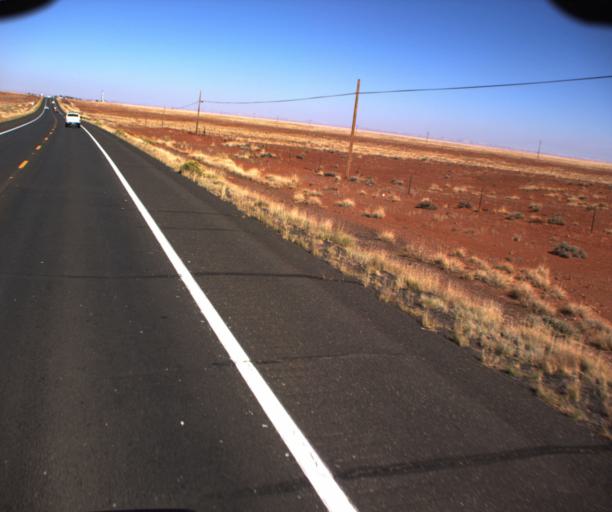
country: US
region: Arizona
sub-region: Coconino County
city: Tuba City
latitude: 35.7217
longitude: -111.4846
